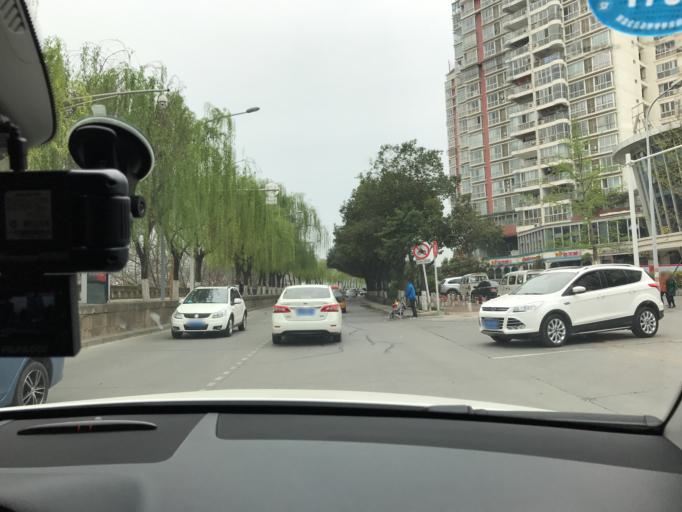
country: CN
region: Sichuan
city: Mianyang
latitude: 31.4522
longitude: 104.7126
